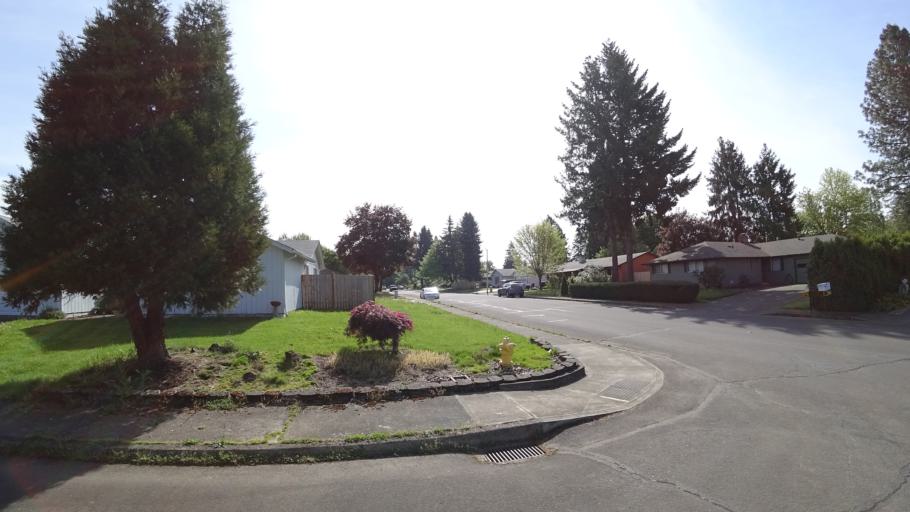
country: US
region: Oregon
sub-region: Washington County
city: Hillsboro
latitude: 45.5210
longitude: -122.9484
